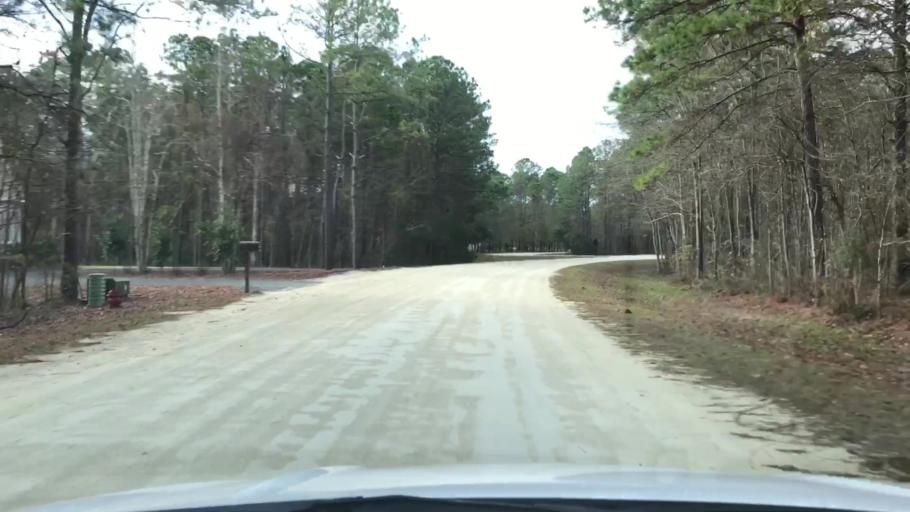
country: US
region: South Carolina
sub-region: Charleston County
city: Isle of Palms
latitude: 32.9033
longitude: -79.7243
